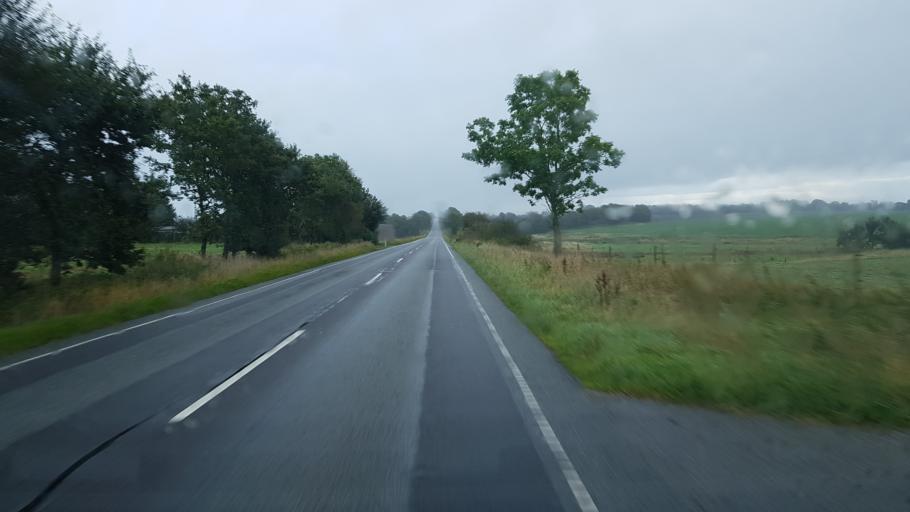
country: DK
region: South Denmark
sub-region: Kolding Kommune
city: Vamdrup
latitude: 55.3469
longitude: 9.2557
